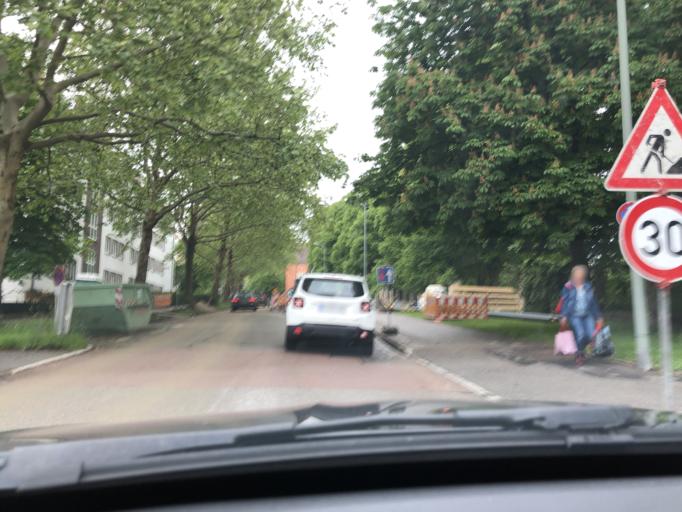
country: DE
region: Bavaria
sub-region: Upper Bavaria
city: Freising
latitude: 48.4084
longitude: 11.7514
